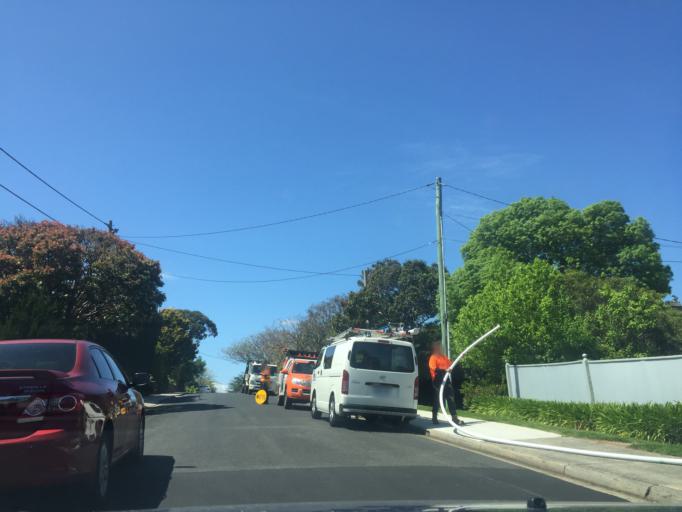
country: AU
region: Victoria
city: Ivanhoe East
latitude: -37.7705
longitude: 145.0548
